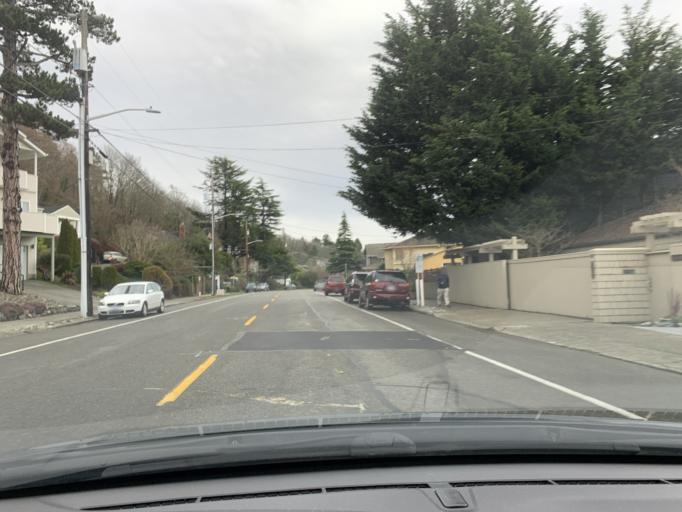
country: US
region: Washington
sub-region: King County
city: White Center
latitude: 47.5562
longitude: -122.4002
